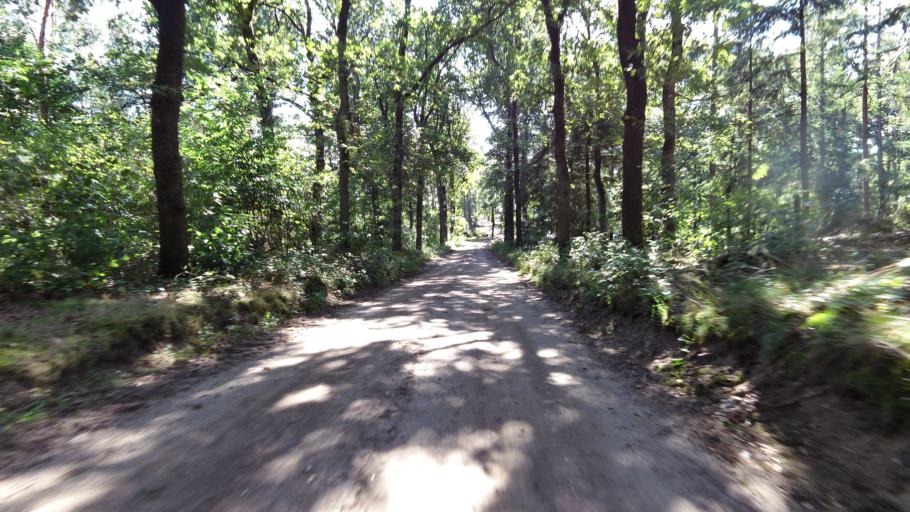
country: NL
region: Gelderland
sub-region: Gemeente Renkum
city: Renkum
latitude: 51.9985
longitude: 5.7393
